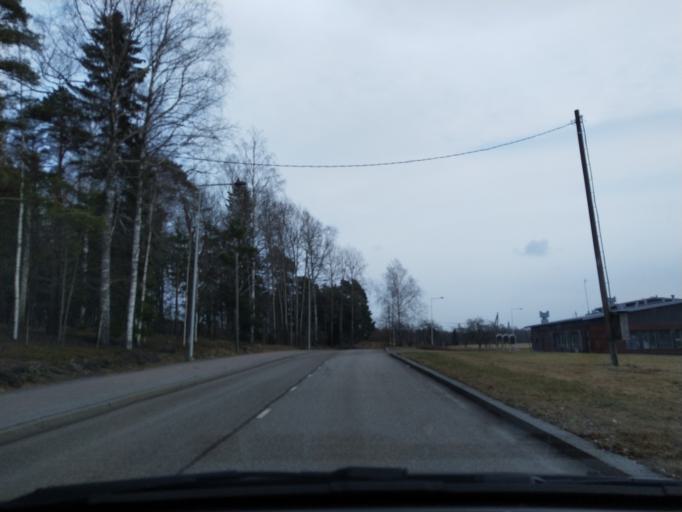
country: FI
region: Uusimaa
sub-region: Helsinki
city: Vantaa
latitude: 60.3032
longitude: 25.0076
